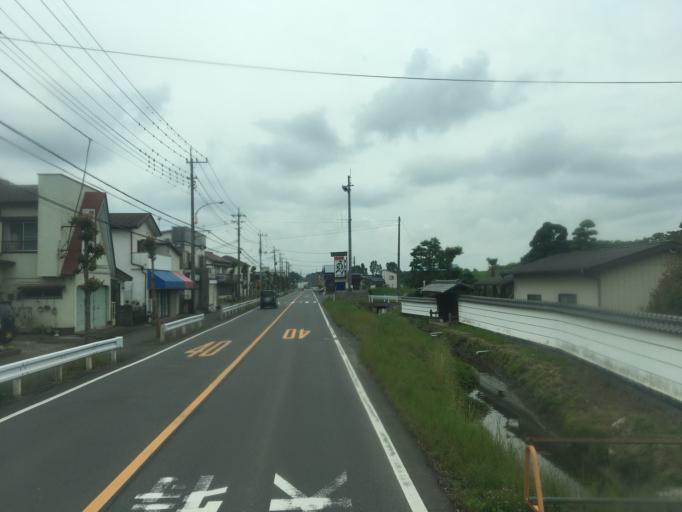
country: JP
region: Saitama
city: Kawagoe
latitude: 35.9740
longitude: 139.4620
